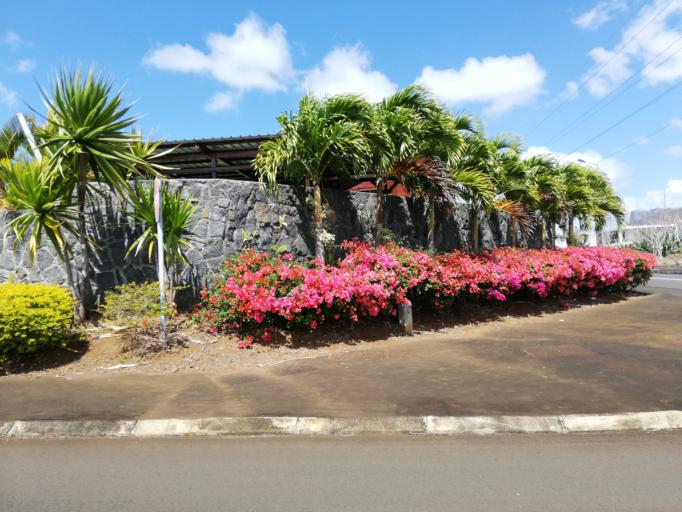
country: MU
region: Plaines Wilhems
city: Ebene
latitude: -20.2301
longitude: 57.4809
